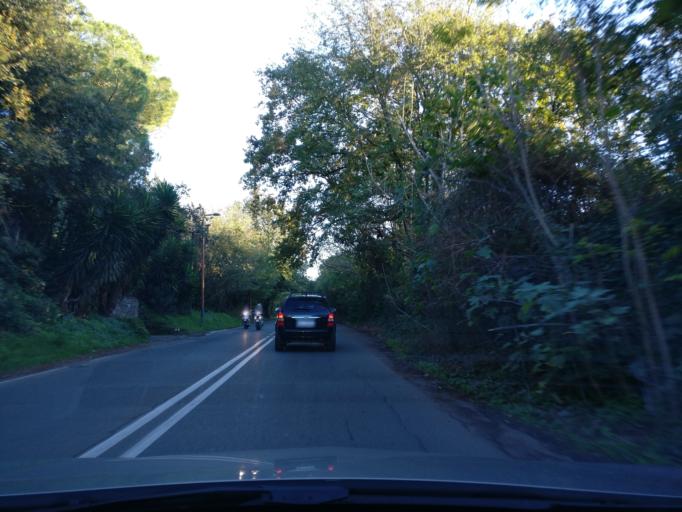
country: IT
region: Latium
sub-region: Citta metropolitana di Roma Capitale
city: Rome
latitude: 41.8545
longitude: 12.5259
